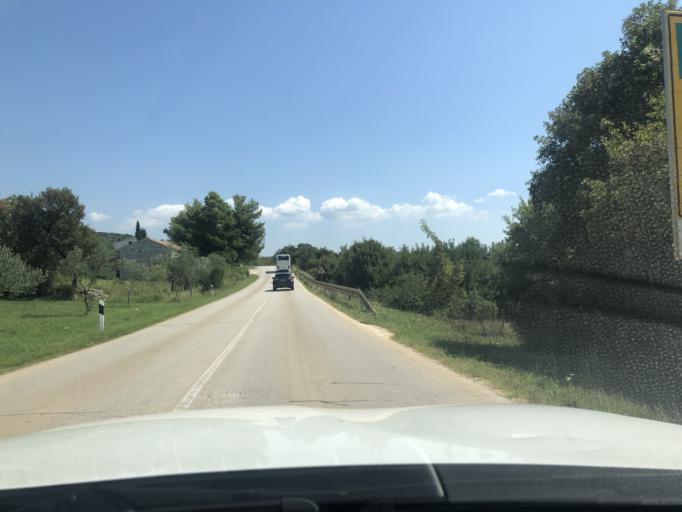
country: HR
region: Istarska
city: Vodnjan
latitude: 45.0363
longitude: 13.7871
